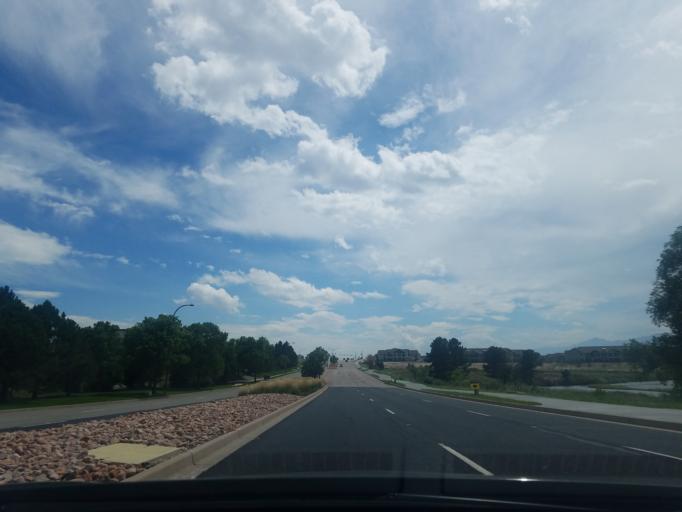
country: US
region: Colorado
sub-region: El Paso County
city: Gleneagle
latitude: 38.9996
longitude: -104.7980
